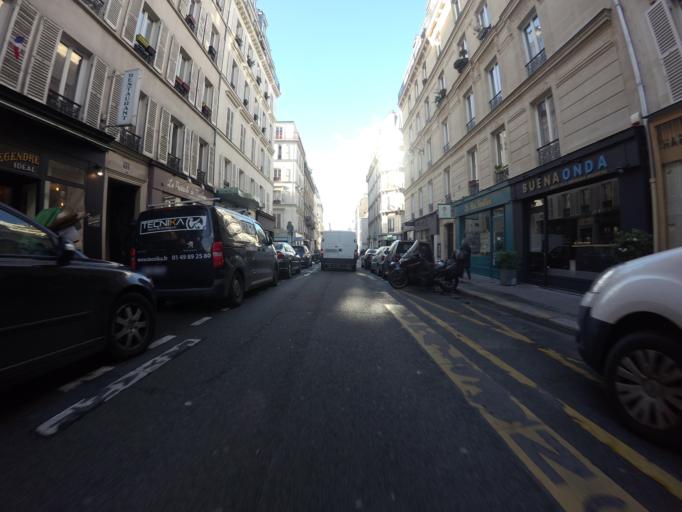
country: FR
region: Ile-de-France
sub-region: Departement des Hauts-de-Seine
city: Clichy
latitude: 48.8874
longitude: 2.3197
